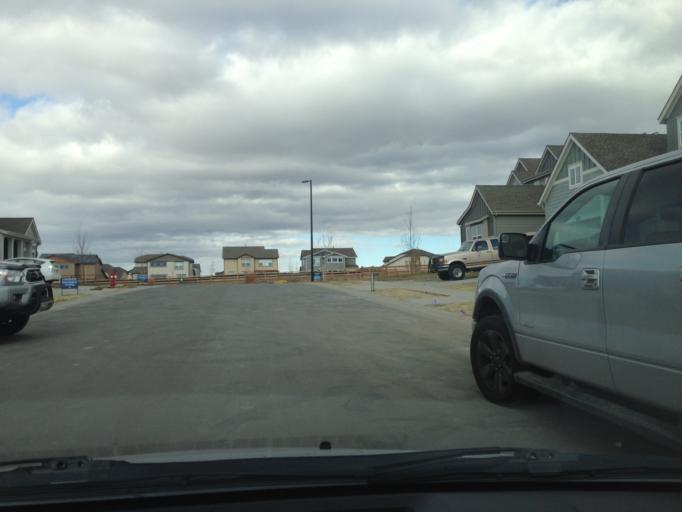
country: US
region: Colorado
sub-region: Boulder County
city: Lafayette
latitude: 40.0283
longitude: -105.0845
